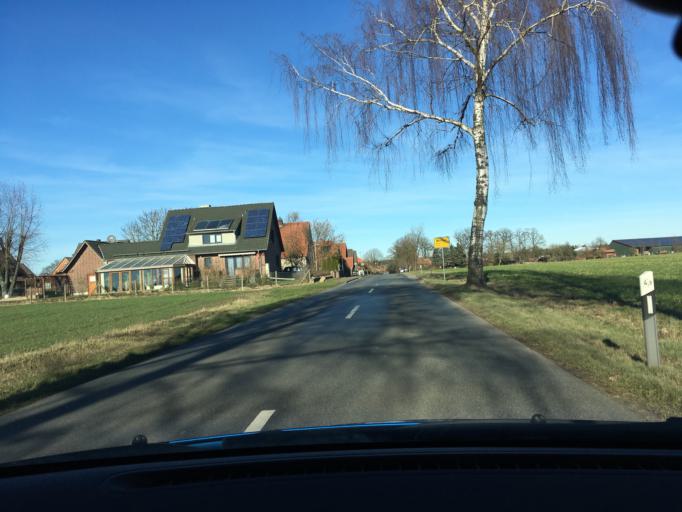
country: DE
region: Lower Saxony
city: Schwienau
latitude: 53.0015
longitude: 10.4444
